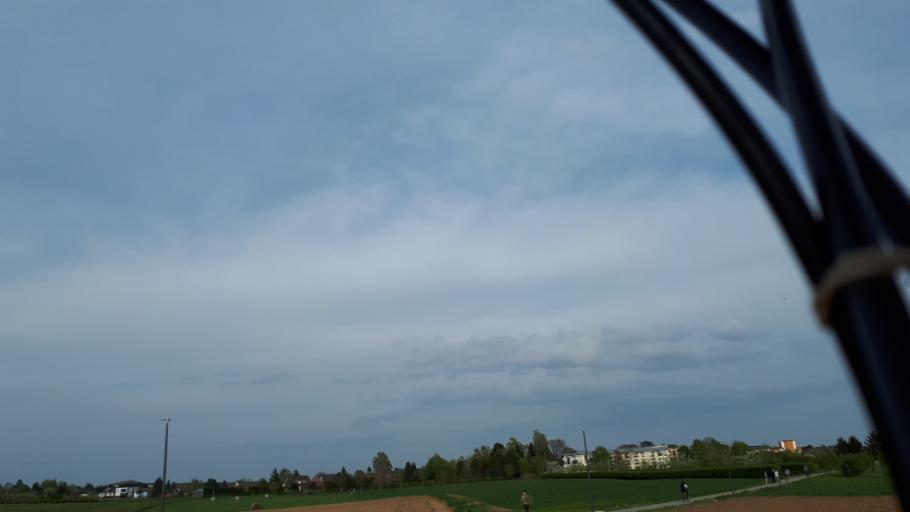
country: LU
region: Luxembourg
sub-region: Canton de Luxembourg
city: Bertrange
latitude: 49.6169
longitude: 6.0398
